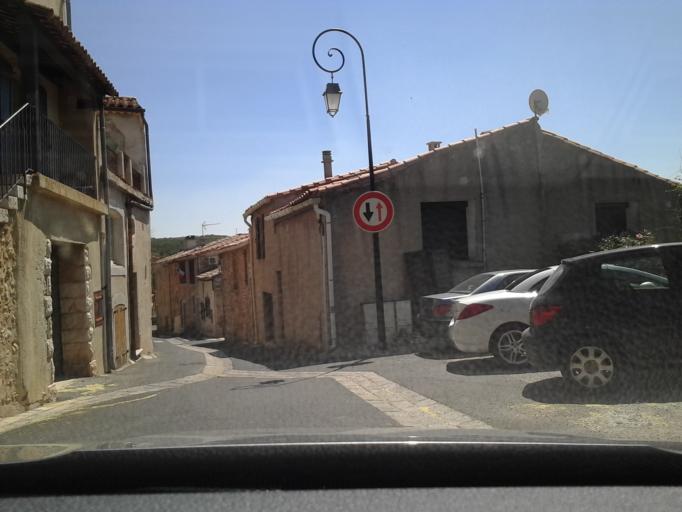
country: FR
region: Languedoc-Roussillon
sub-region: Departement de l'Herault
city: Montpeyroux
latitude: 43.7110
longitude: 3.4838
